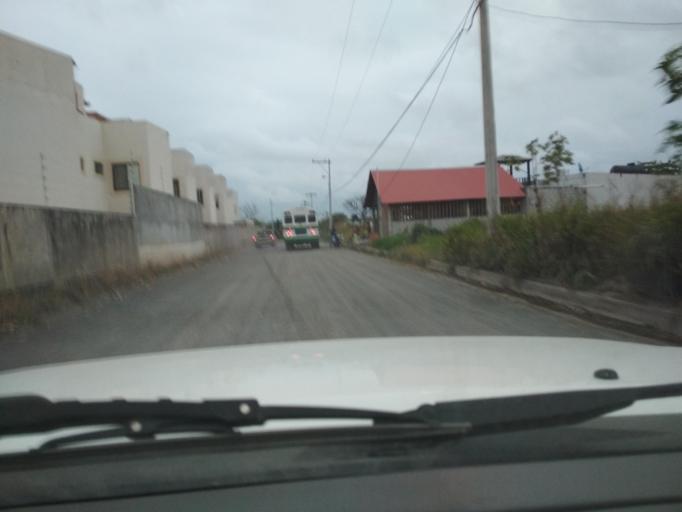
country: MX
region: Veracruz
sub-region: Medellin
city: Fraccionamiento Arboledas San Ramon
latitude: 19.0887
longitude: -96.1297
